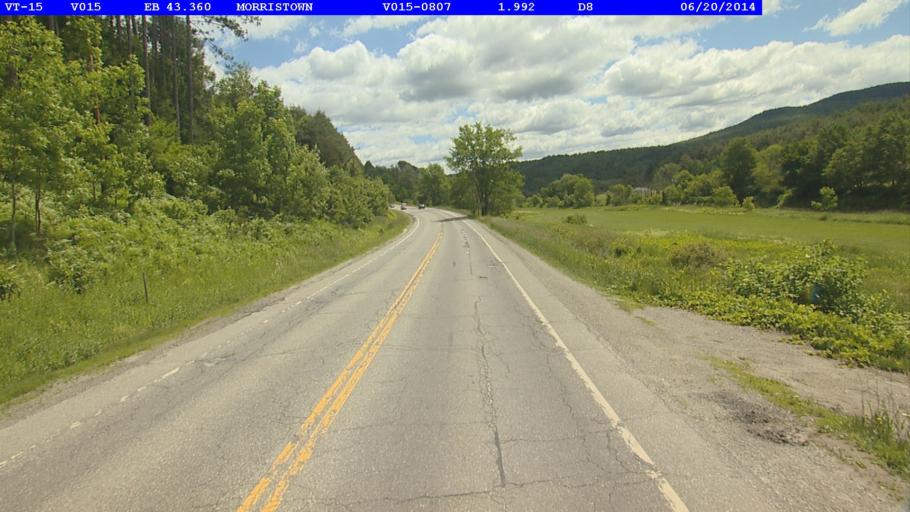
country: US
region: Vermont
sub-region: Lamoille County
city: Morrisville
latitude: 44.5676
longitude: -72.5745
